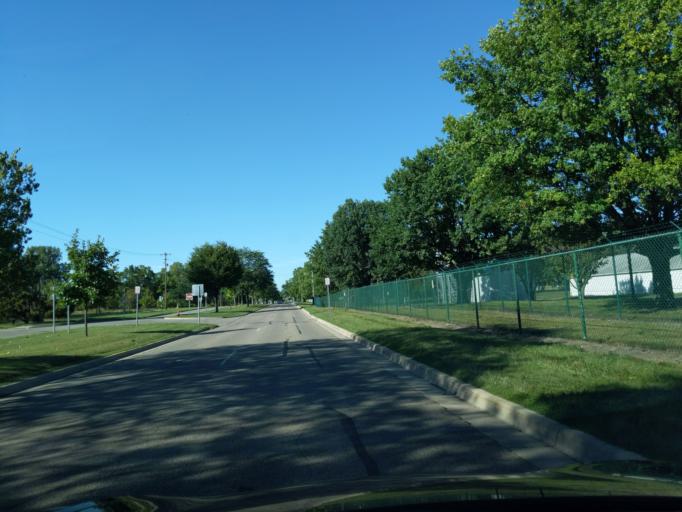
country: US
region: Michigan
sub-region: Ingham County
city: East Lansing
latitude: 42.7129
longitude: -84.4936
